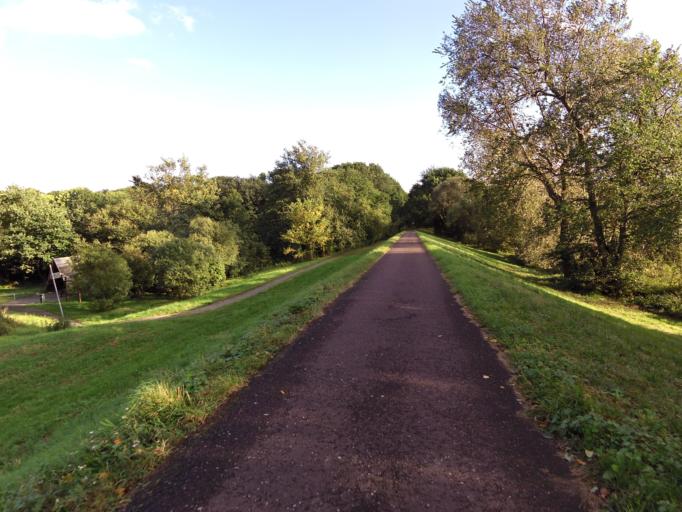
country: DE
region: Saxony-Anhalt
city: Magdeburg
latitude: 52.0860
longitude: 11.6834
